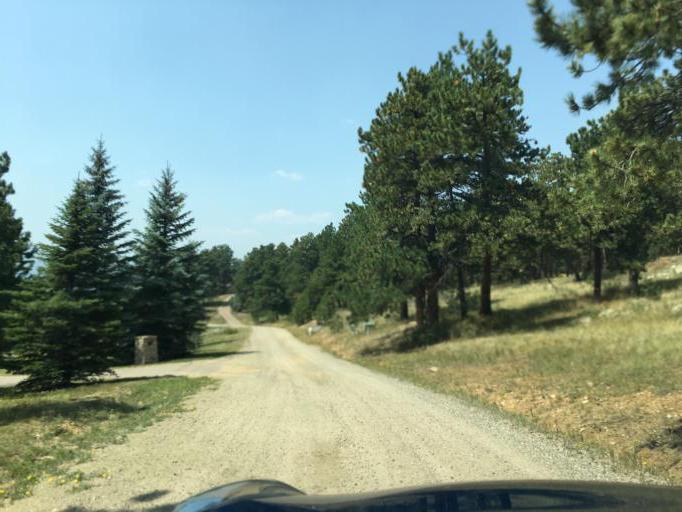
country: US
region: Colorado
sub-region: Jefferson County
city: Genesee
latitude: 39.7174
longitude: -105.3000
